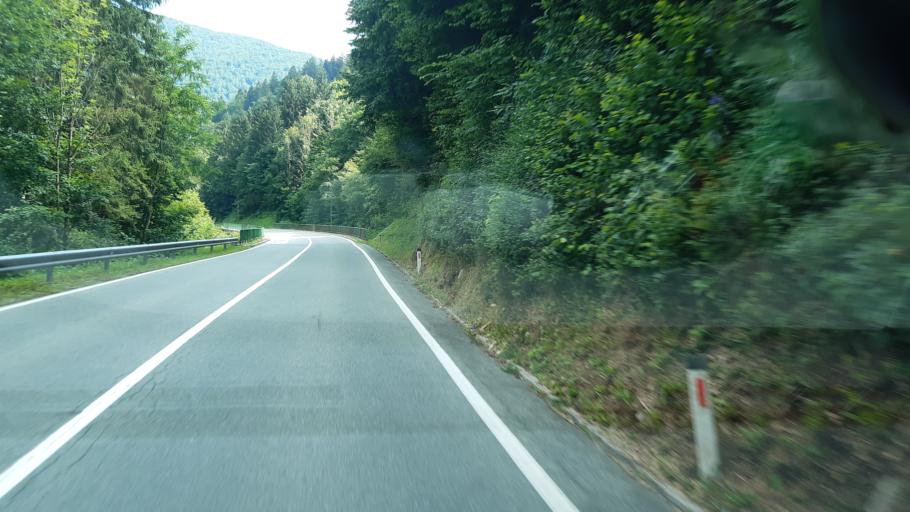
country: SI
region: Trzic
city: Trzic
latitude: 46.3721
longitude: 14.3023
